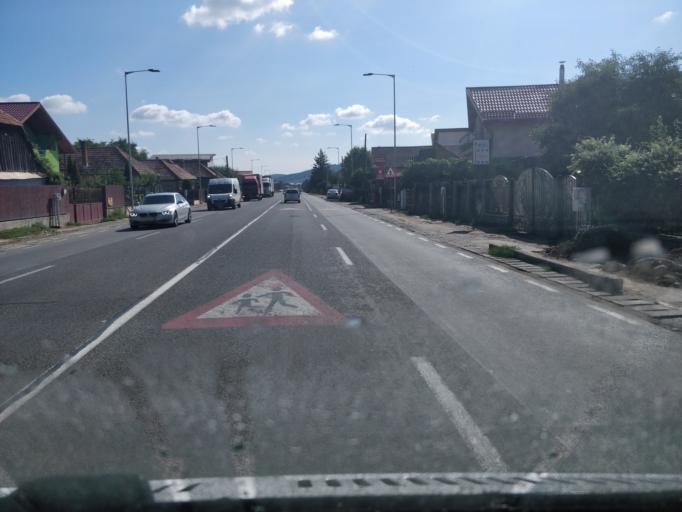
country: RO
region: Cluj
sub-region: Comuna Floresti
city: Floresti
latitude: 46.7441
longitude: 23.4660
